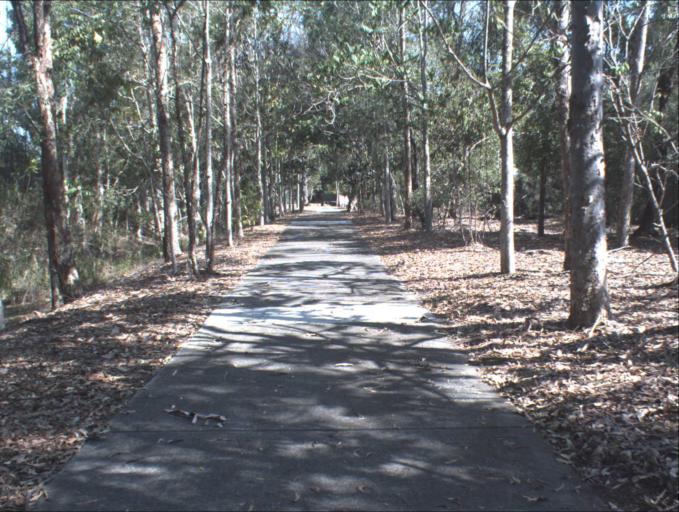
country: AU
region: Queensland
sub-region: Logan
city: Beenleigh
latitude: -27.6874
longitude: 153.1883
